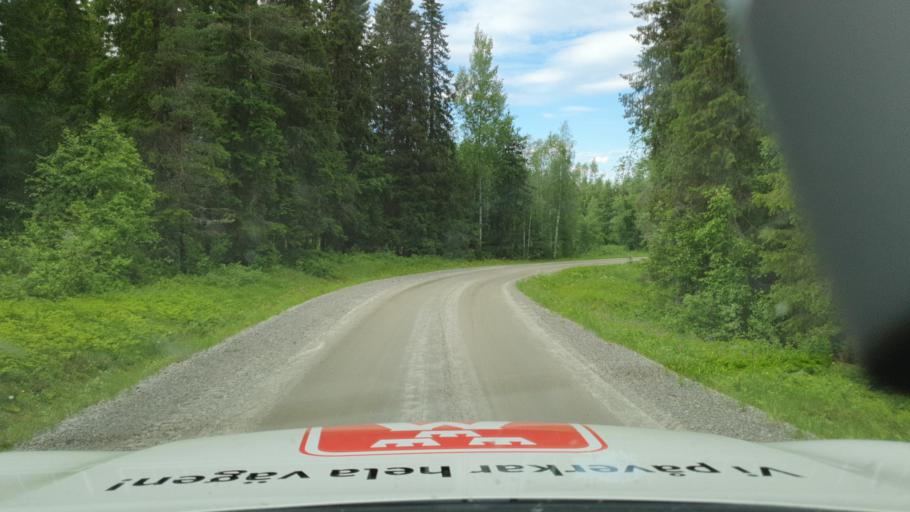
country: SE
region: Vaesterbotten
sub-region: Norsjo Kommun
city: Norsjoe
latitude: 64.8048
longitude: 19.6639
